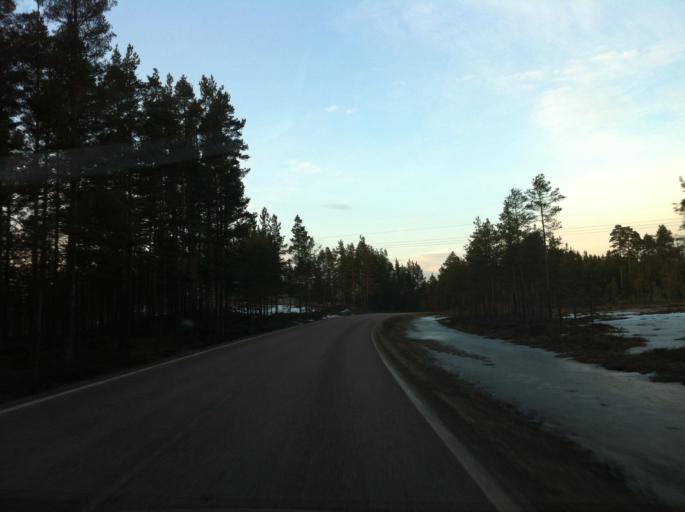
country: SE
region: Dalarna
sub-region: Vansbro Kommun
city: Vansbro
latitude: 60.5401
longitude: 14.2066
